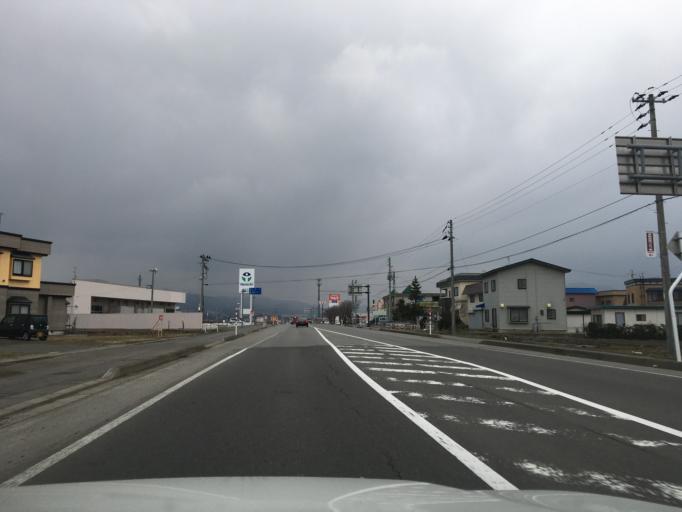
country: JP
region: Aomori
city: Kuroishi
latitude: 40.5836
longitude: 140.5687
